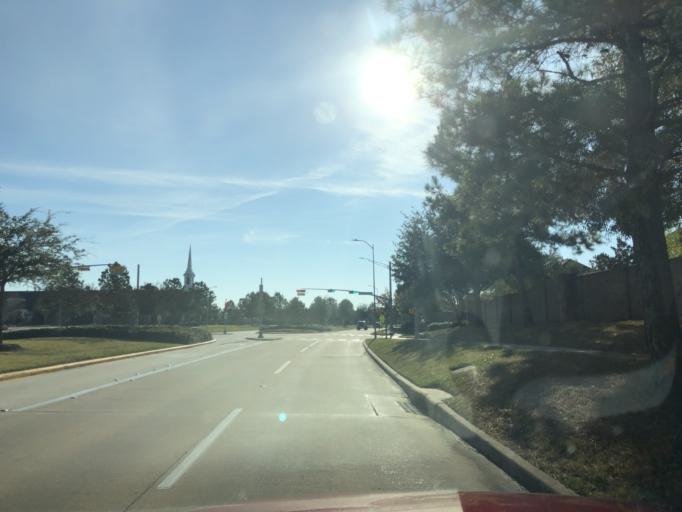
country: US
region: Texas
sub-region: Harris County
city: Tomball
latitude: 30.0538
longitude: -95.5694
